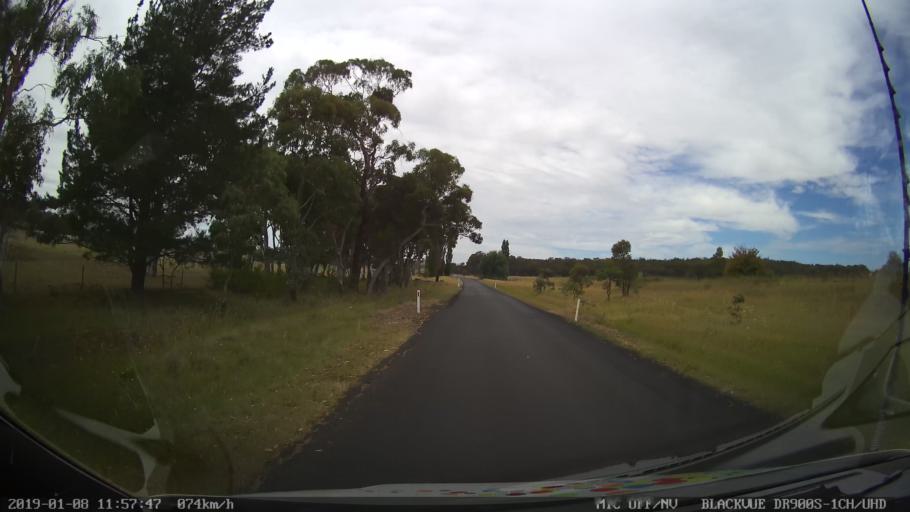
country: AU
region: New South Wales
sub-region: Armidale Dumaresq
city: Armidale
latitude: -30.4530
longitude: 151.5693
